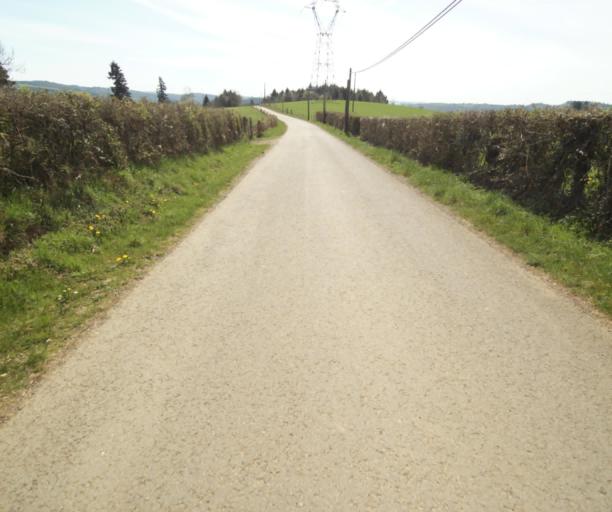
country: FR
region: Limousin
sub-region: Departement de la Correze
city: Naves
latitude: 45.3678
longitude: 1.8027
